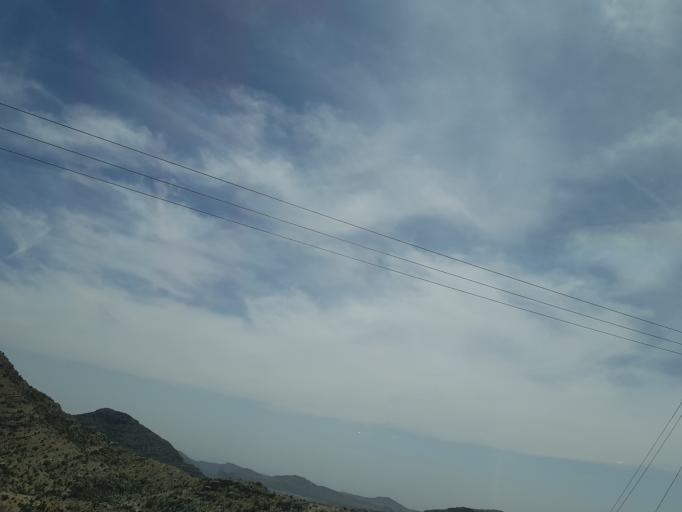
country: OM
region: Muhafazat ad Dakhiliyah
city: Nizwa
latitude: 23.1158
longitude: 57.6397
